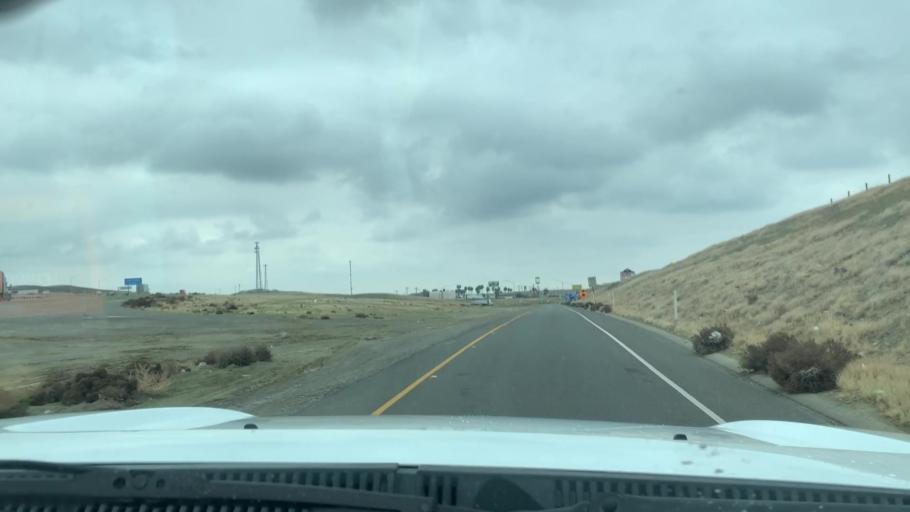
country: US
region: California
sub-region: Kings County
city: Kettleman City
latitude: 35.9804
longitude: -119.9583
